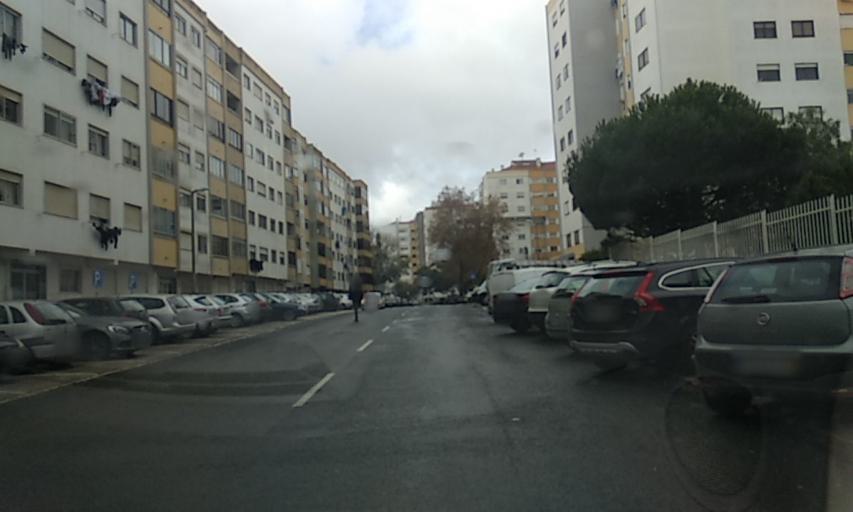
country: PT
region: Lisbon
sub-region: Sintra
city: Cacem
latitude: 38.7545
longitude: -9.2845
